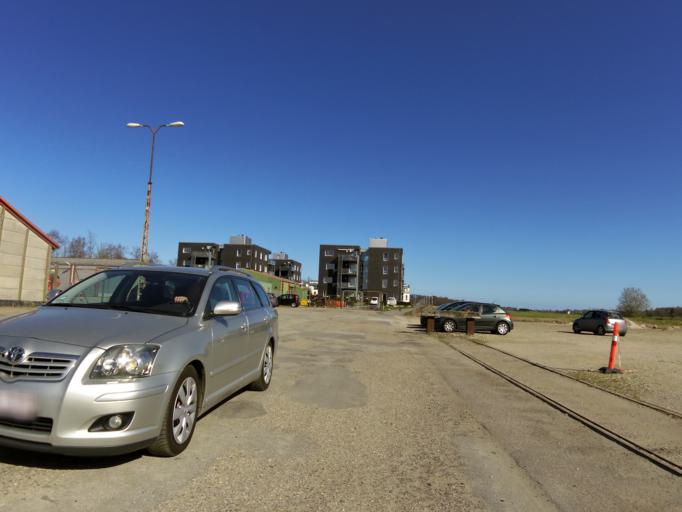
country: DK
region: South Denmark
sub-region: Haderslev Kommune
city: Haderslev
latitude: 55.2525
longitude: 9.5097
